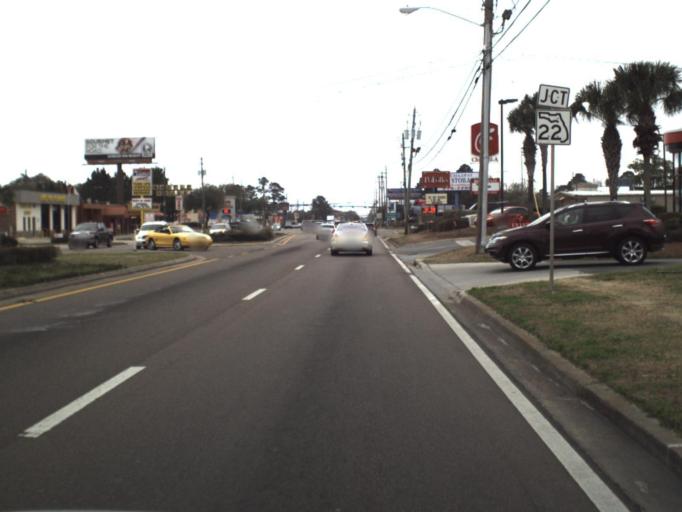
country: US
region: Florida
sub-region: Bay County
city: Springfield
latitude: 30.1555
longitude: -85.5912
